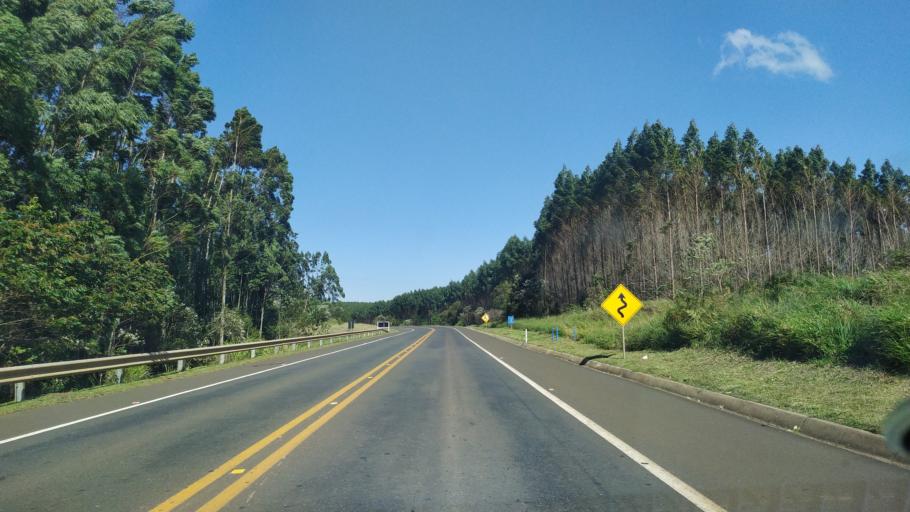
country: BR
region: Parana
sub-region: Ortigueira
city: Ortigueira
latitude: -24.2487
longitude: -50.7768
